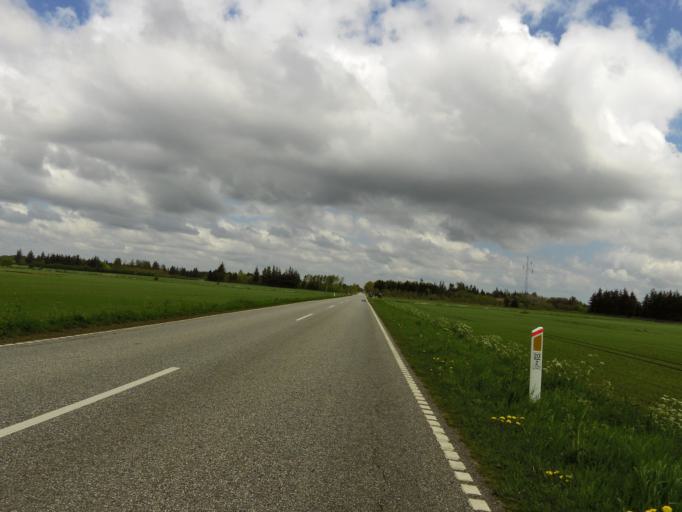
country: DK
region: South Denmark
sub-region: Haderslev Kommune
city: Gram
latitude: 55.2542
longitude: 8.9840
